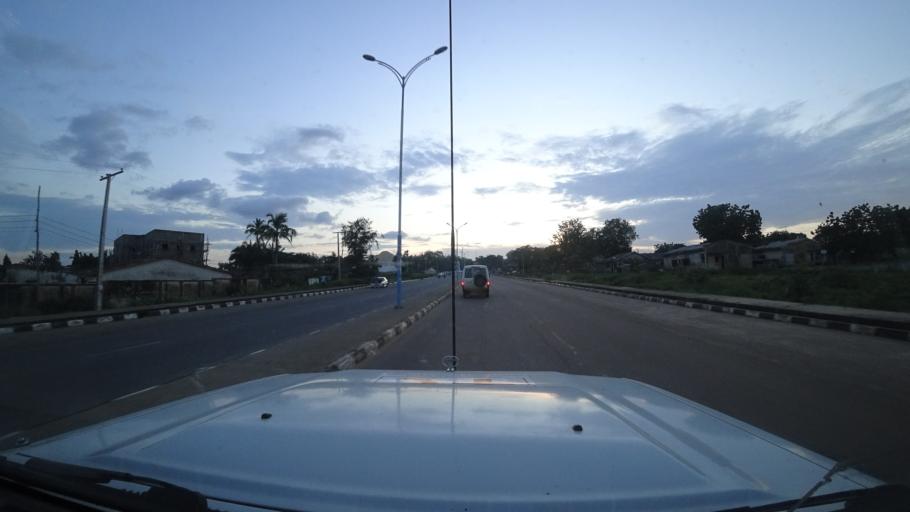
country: NG
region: Niger
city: Minna
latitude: 9.6401
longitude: 6.5436
